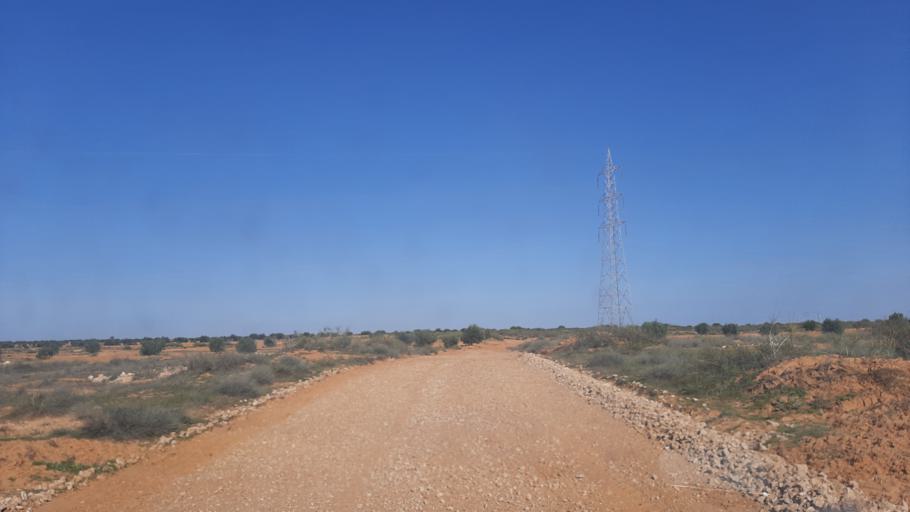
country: TN
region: Madanin
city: Medenine
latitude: 33.2782
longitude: 10.7744
